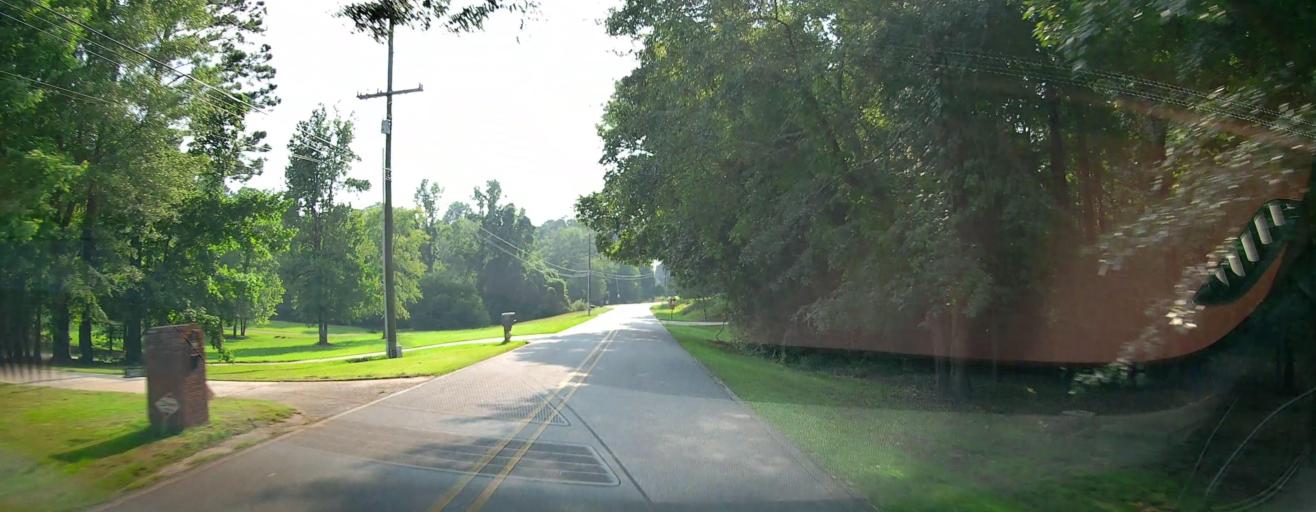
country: US
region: Georgia
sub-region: Bibb County
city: Macon
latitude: 32.9450
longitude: -83.7285
